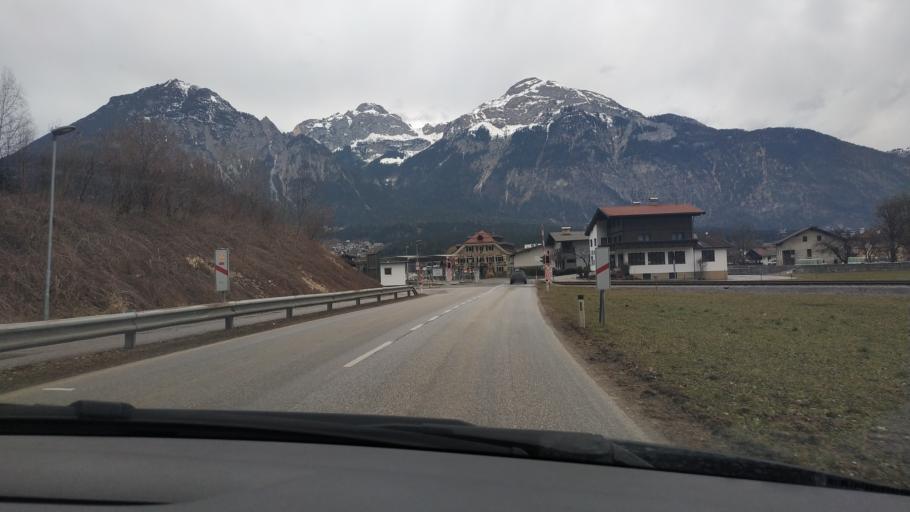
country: AT
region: Tyrol
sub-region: Politischer Bezirk Schwaz
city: Strass im Zillertal
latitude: 47.3940
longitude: 11.8196
